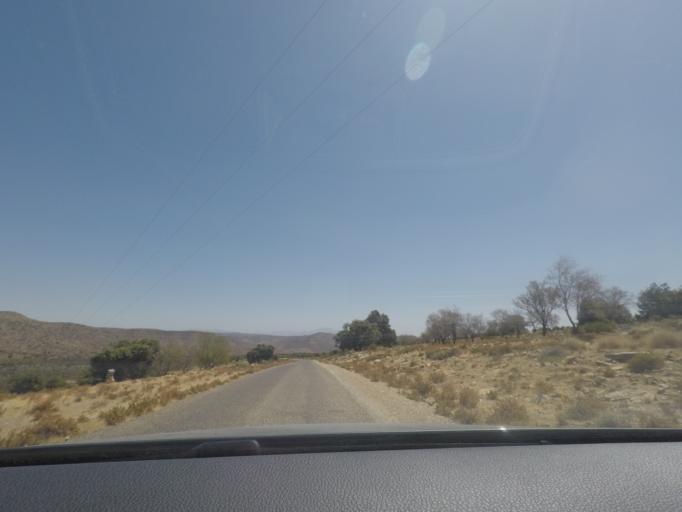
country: MA
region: Souss-Massa-Draa
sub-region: Agadir-Ida-ou-Tnan
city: Tadrart
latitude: 30.7374
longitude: -9.3660
